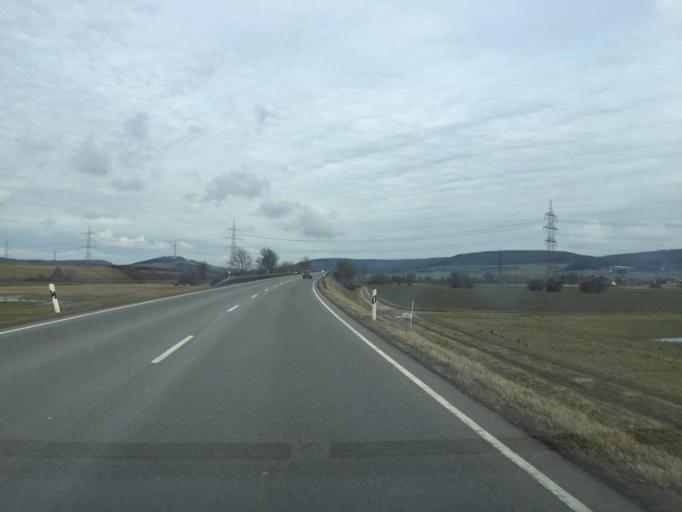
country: DE
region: Baden-Wuerttemberg
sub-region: Freiburg Region
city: Donaueschingen
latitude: 47.9277
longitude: 8.5476
